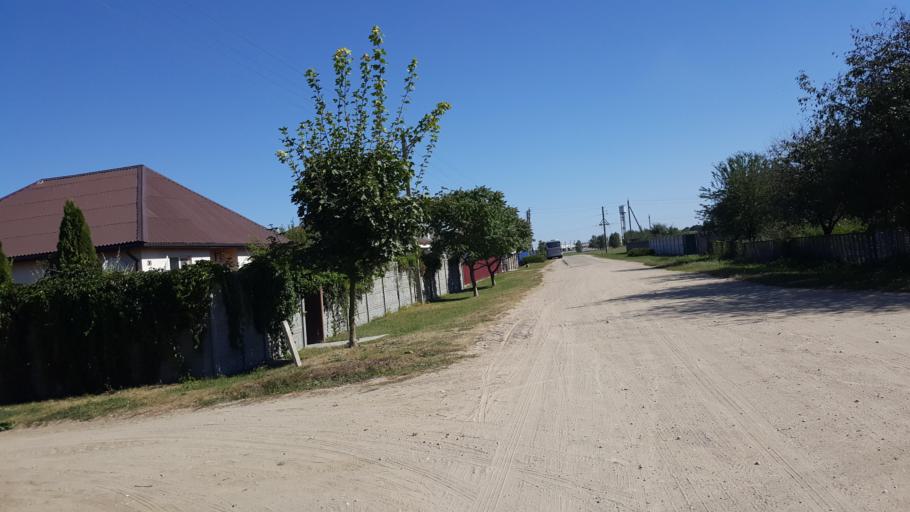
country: BY
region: Brest
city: Vysokaye
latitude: 52.2637
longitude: 23.4999
